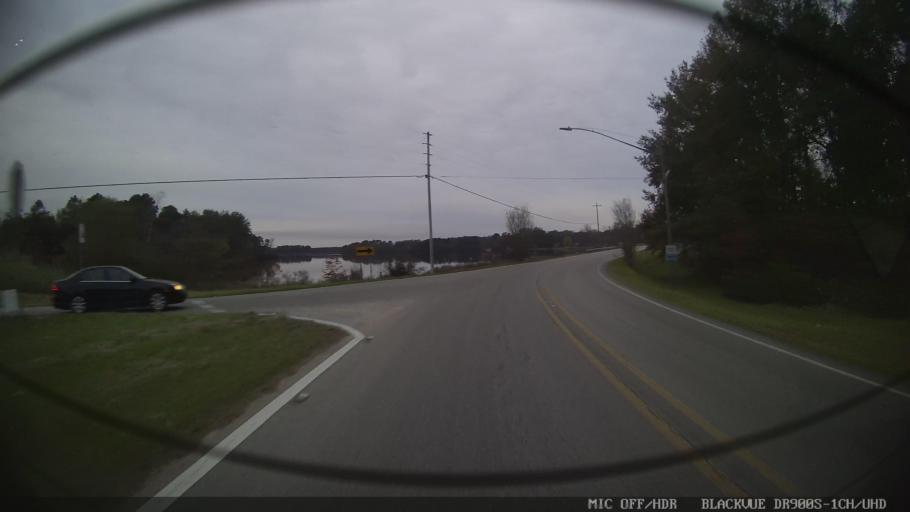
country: US
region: Mississippi
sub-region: Clarke County
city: Quitman
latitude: 32.0397
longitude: -88.7086
